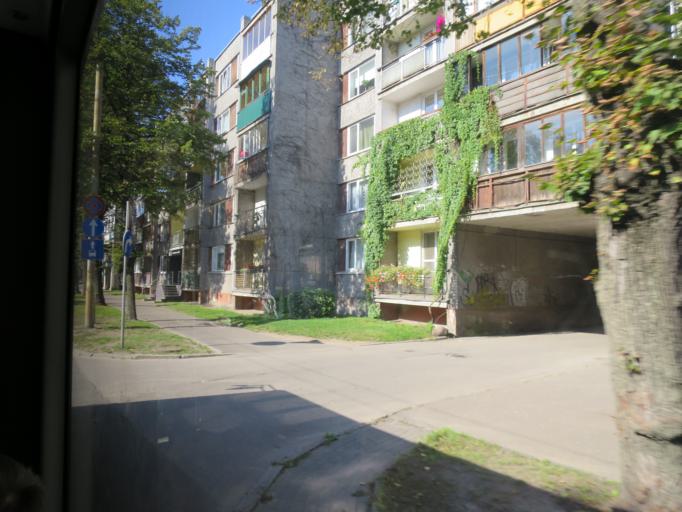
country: LV
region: Riga
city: Jaunciems
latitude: 56.9770
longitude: 24.1785
